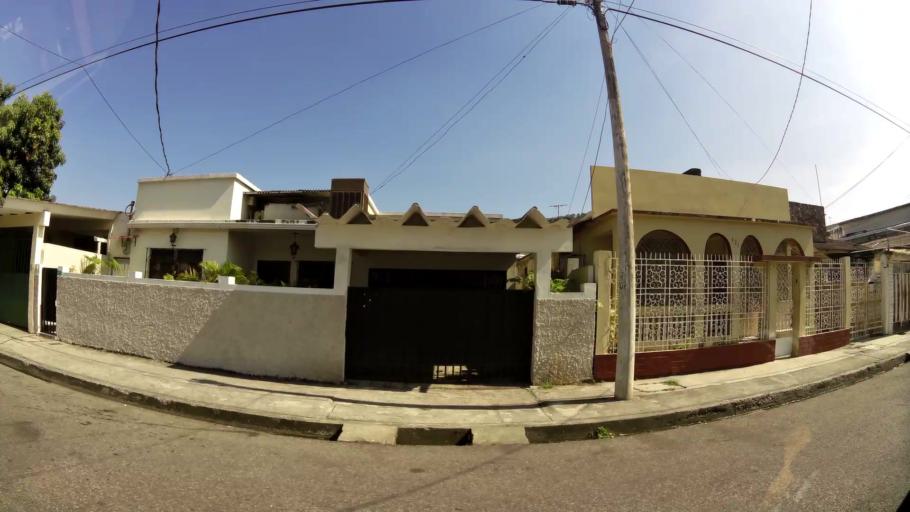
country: EC
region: Guayas
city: Guayaquil
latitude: -2.1627
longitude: -79.9203
